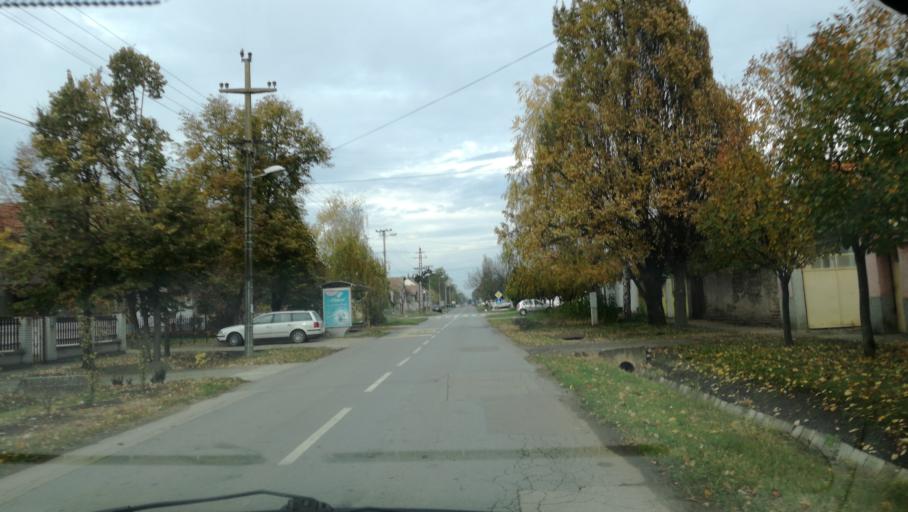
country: RS
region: Autonomna Pokrajina Vojvodina
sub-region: Severnobanatski Okrug
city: Kikinda
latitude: 45.8380
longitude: 20.4734
